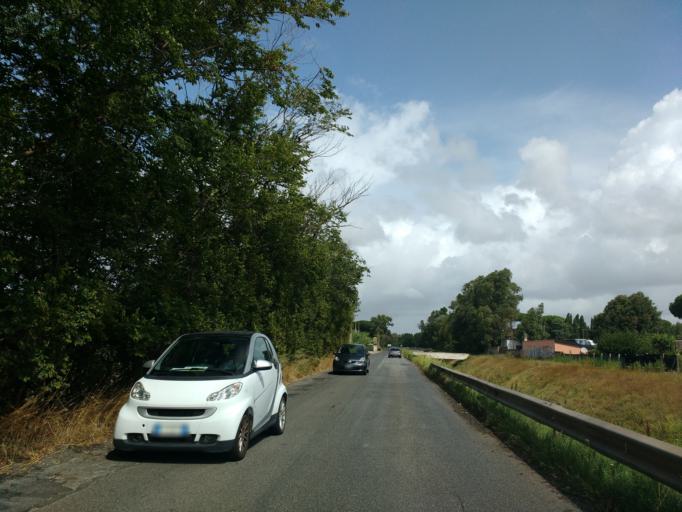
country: IT
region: Latium
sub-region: Citta metropolitana di Roma Capitale
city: Acilia-Castel Fusano-Ostia Antica
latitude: 41.7646
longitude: 12.3266
